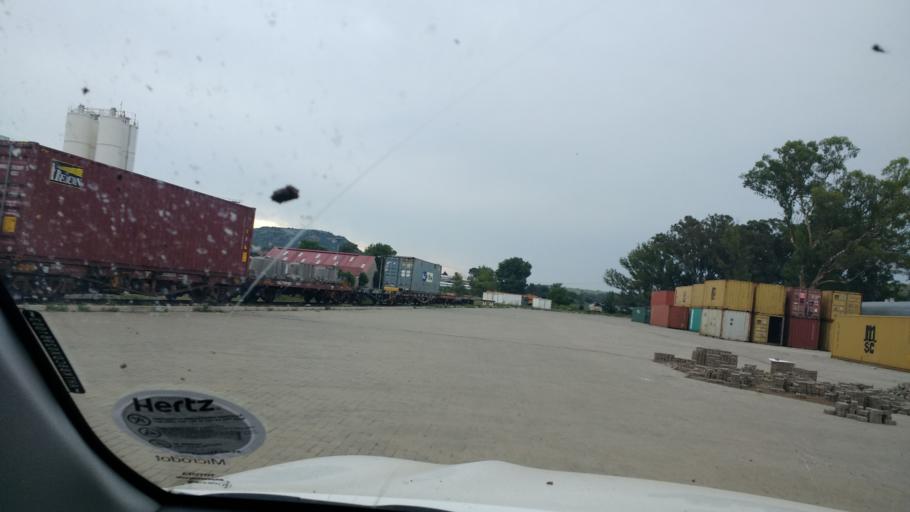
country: LS
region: Maseru
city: Maseru
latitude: -29.2979
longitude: 27.4688
